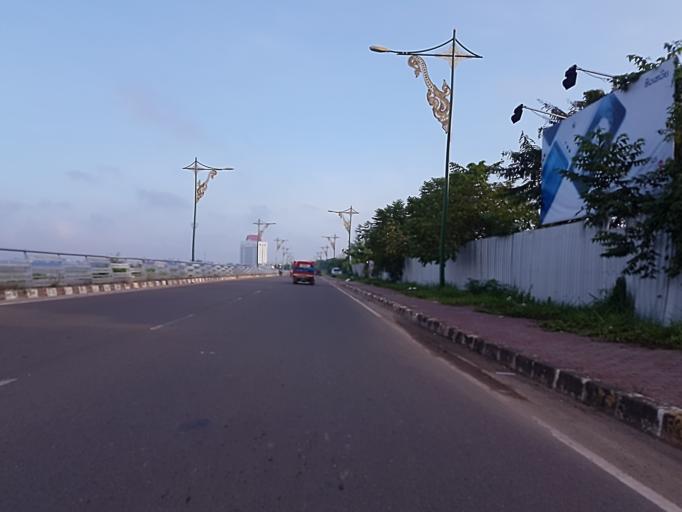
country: LA
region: Vientiane
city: Vientiane
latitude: 17.9457
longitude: 102.6160
